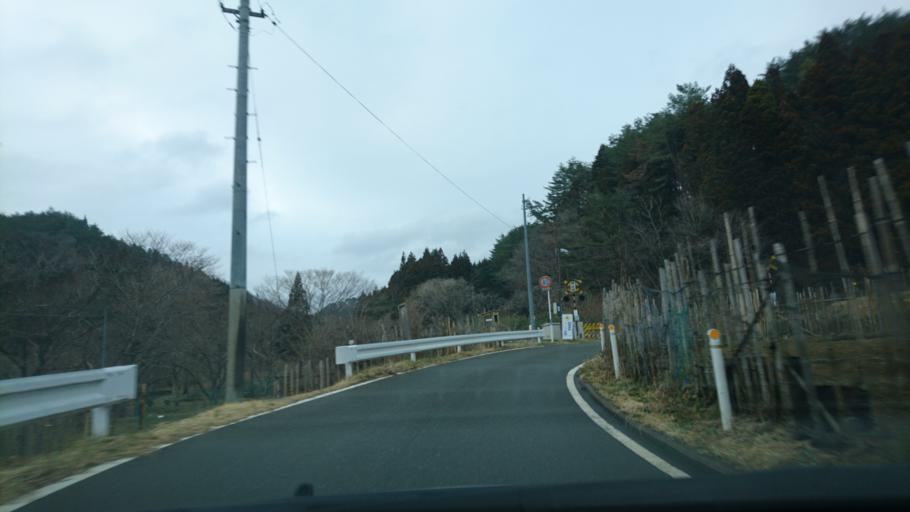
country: JP
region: Iwate
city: Ofunato
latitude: 38.9861
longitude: 141.5532
